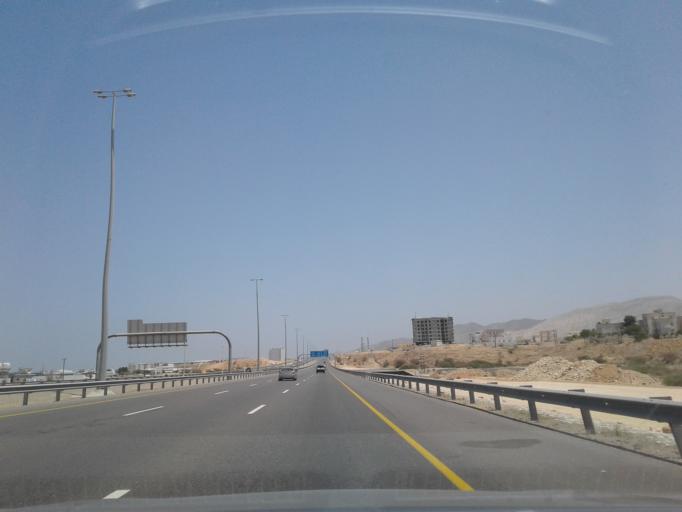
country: OM
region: Muhafazat Masqat
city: Bawshar
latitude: 23.5646
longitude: 58.3572
